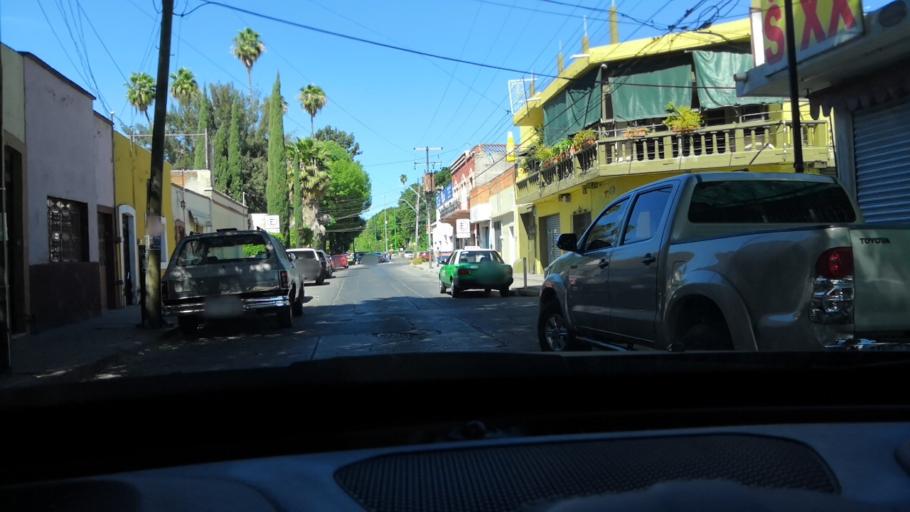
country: MX
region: Guanajuato
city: Leon
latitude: 21.1297
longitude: -101.6849
